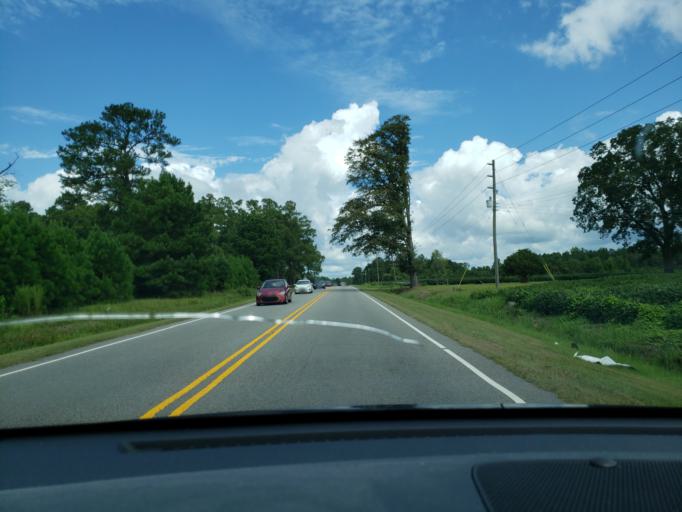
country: US
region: North Carolina
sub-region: Columbus County
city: Brunswick
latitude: 34.2268
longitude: -78.7542
